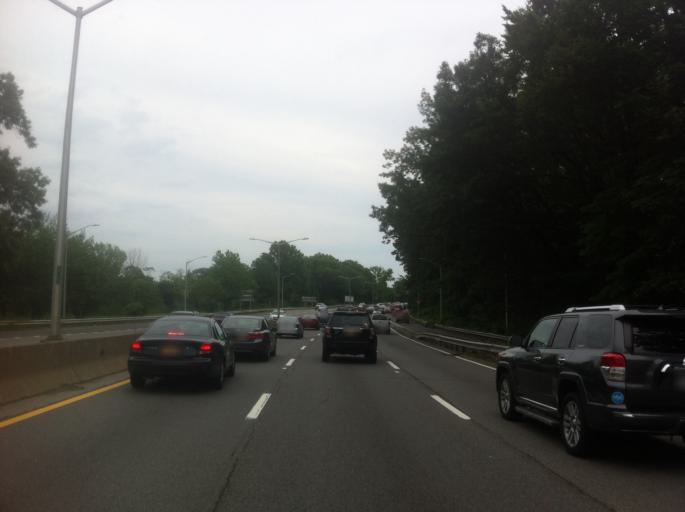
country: US
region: New York
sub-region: Nassau County
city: East Atlantic Beach
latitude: 40.7894
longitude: -73.7814
